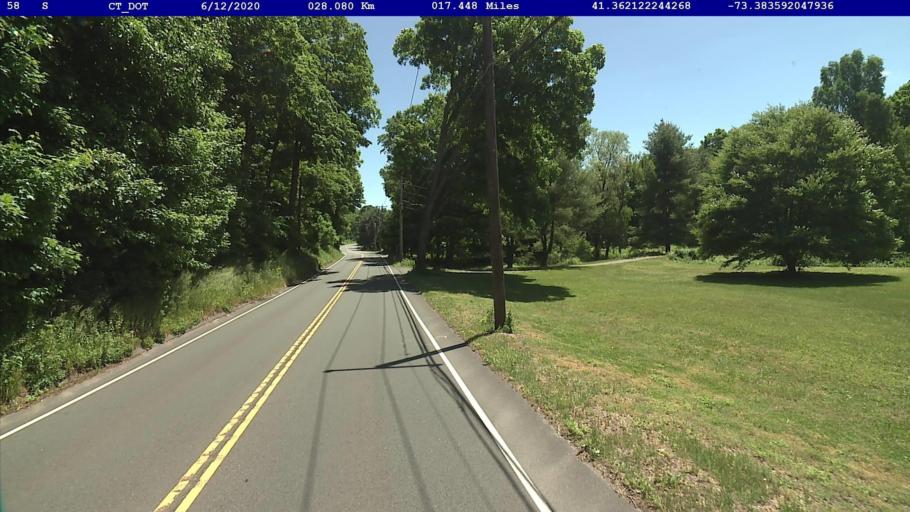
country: US
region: Connecticut
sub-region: Fairfield County
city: Bethel
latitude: 41.3621
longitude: -73.3836
